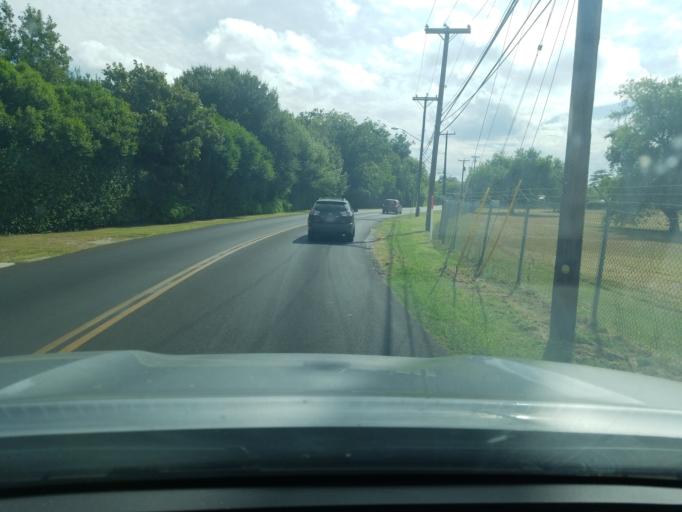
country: US
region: Texas
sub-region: Bexar County
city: Terrell Hills
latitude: 29.4687
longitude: -98.4481
